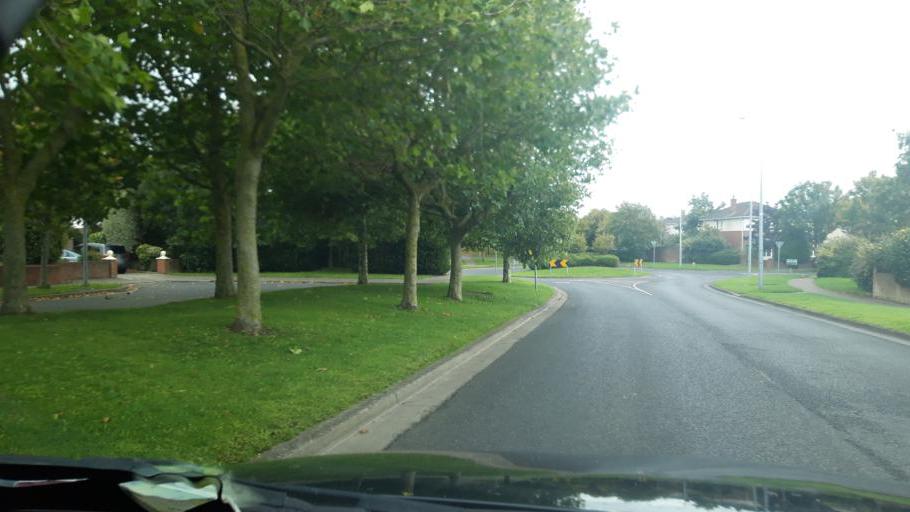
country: IE
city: Knocklyon
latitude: 53.2749
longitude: -6.3281
